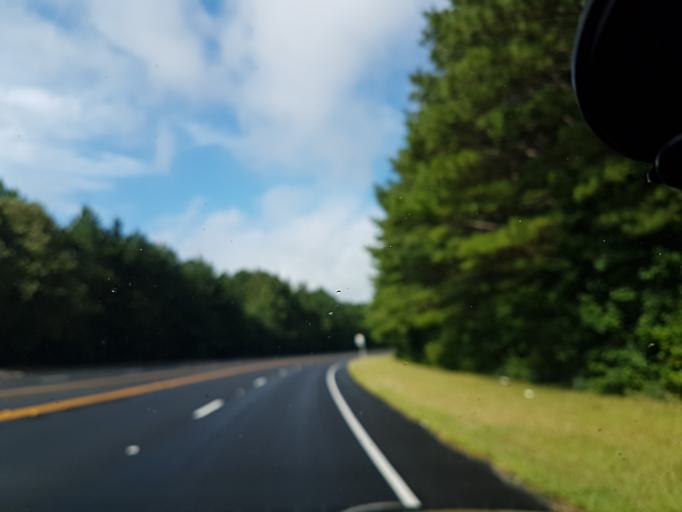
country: US
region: Georgia
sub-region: Fulton County
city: Union City
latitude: 33.5691
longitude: -84.5559
